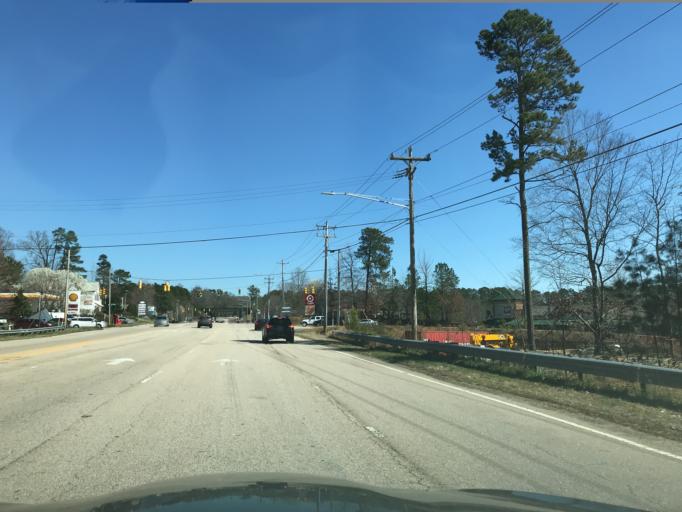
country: US
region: North Carolina
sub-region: Wake County
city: Wake Forest
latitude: 35.9774
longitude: -78.5443
